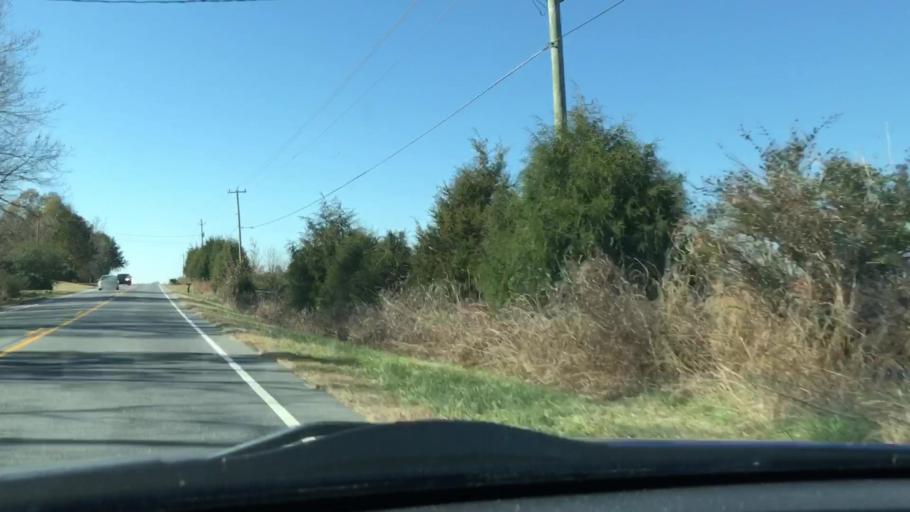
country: US
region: North Carolina
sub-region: Randolph County
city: Asheboro
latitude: 35.6827
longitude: -79.8575
